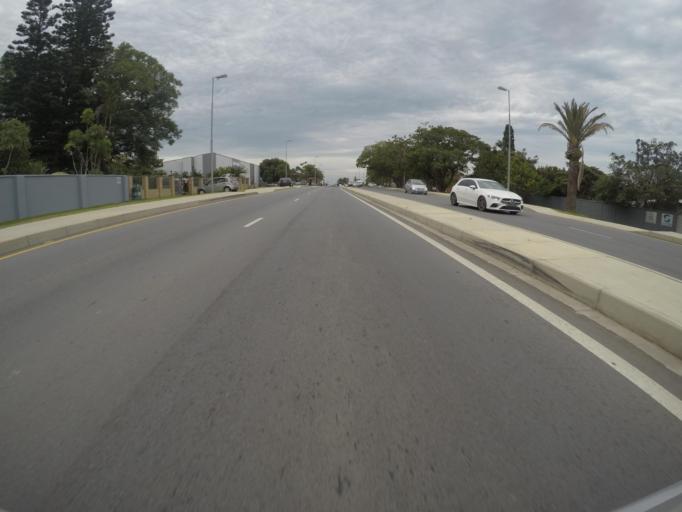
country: ZA
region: Eastern Cape
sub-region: Buffalo City Metropolitan Municipality
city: East London
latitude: -32.9622
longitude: 27.9345
